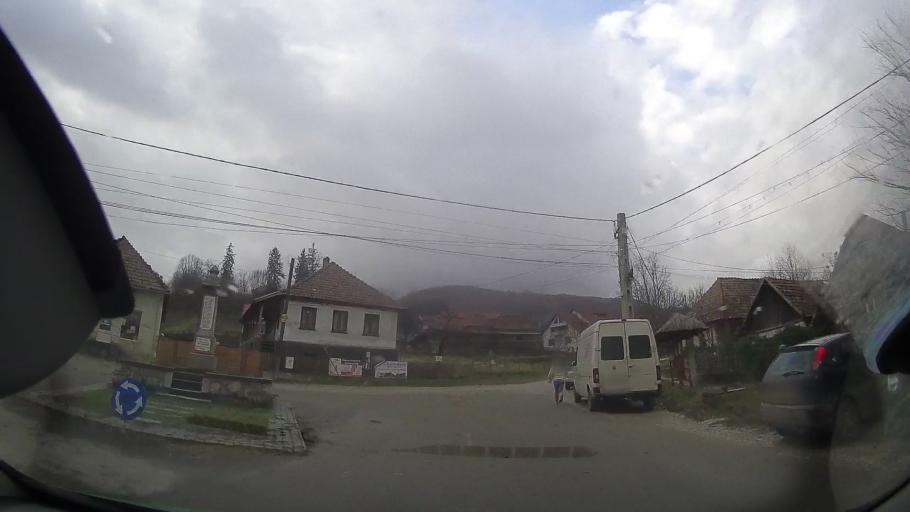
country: RO
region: Cluj
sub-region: Comuna Moldovenesti
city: Moldovenesti
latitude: 46.5013
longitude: 23.6637
